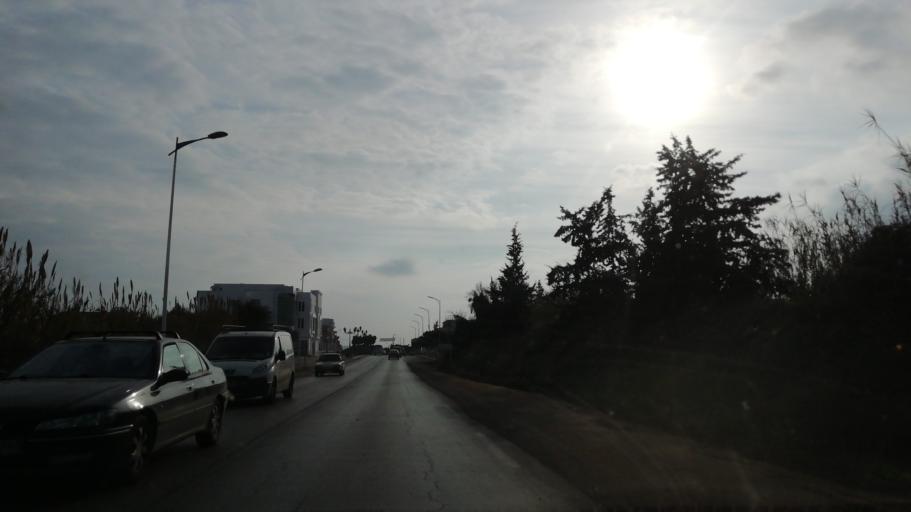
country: DZ
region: Mostaganem
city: Mostaganem
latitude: 35.8681
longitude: 0.0757
